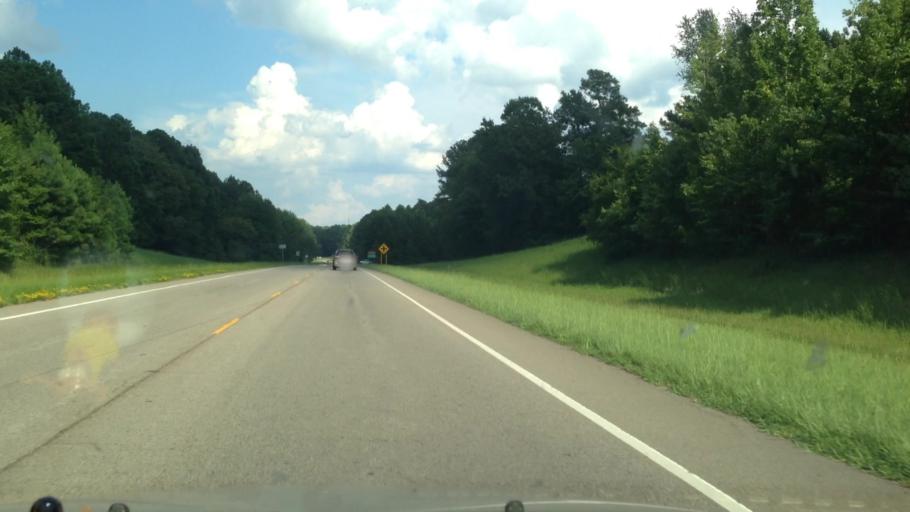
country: US
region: North Carolina
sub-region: Lee County
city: Broadway
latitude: 35.4390
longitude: -79.0708
